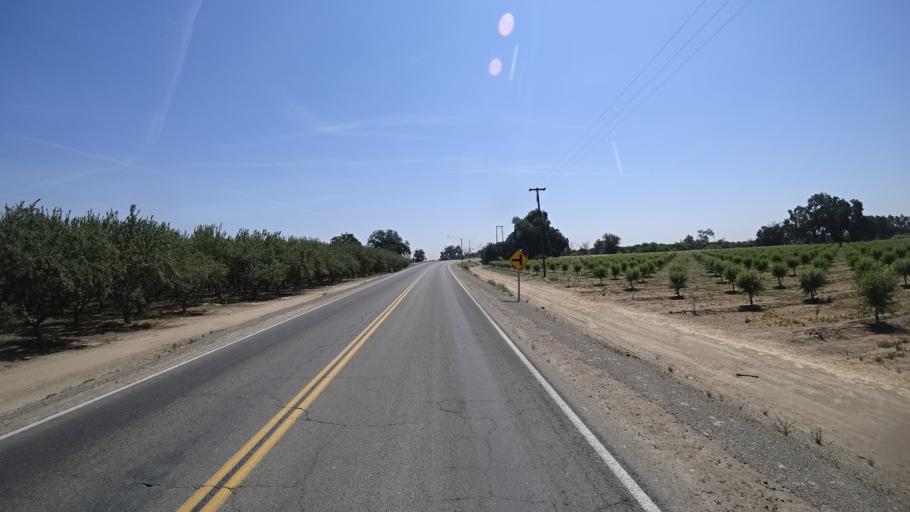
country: US
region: California
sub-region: Fresno County
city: Laton
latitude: 36.4020
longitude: -119.7553
